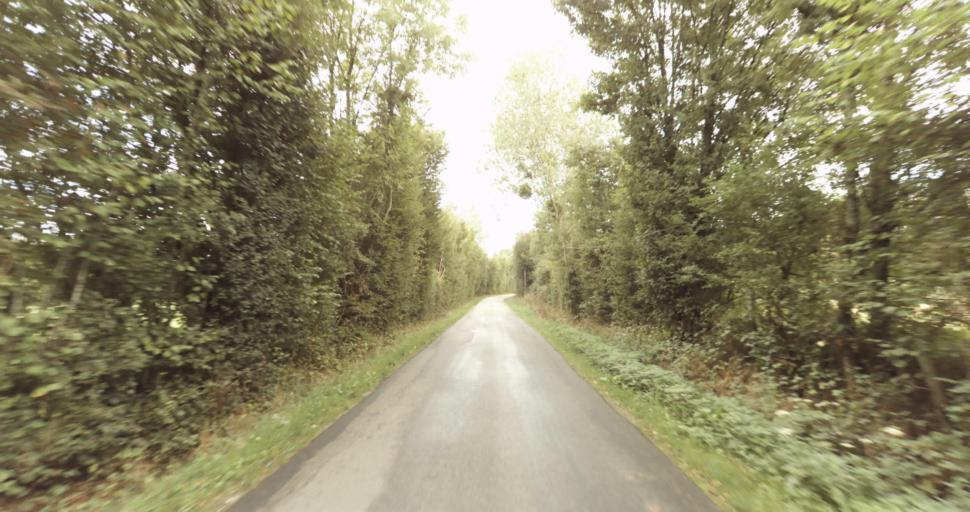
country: FR
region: Lower Normandy
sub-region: Departement de l'Orne
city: Sainte-Gauburge-Sainte-Colombe
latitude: 48.7058
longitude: 0.3571
